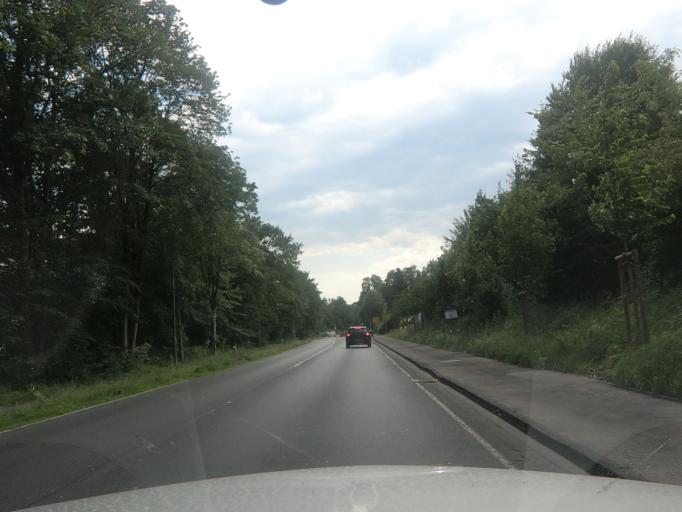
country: DE
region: North Rhine-Westphalia
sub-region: Regierungsbezirk Arnsberg
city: Olpe
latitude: 51.0389
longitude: 7.8607
